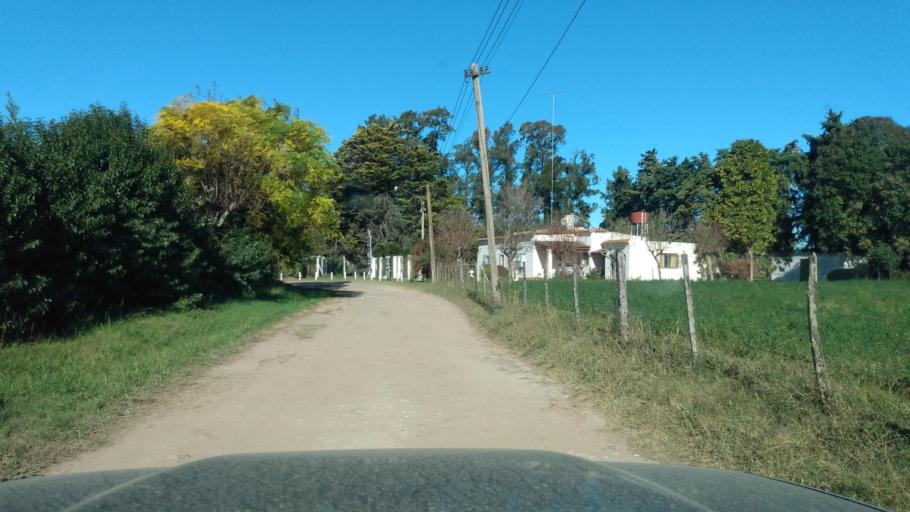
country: AR
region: Buenos Aires
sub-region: Partido de Lujan
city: Lujan
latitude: -34.4853
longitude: -59.2238
